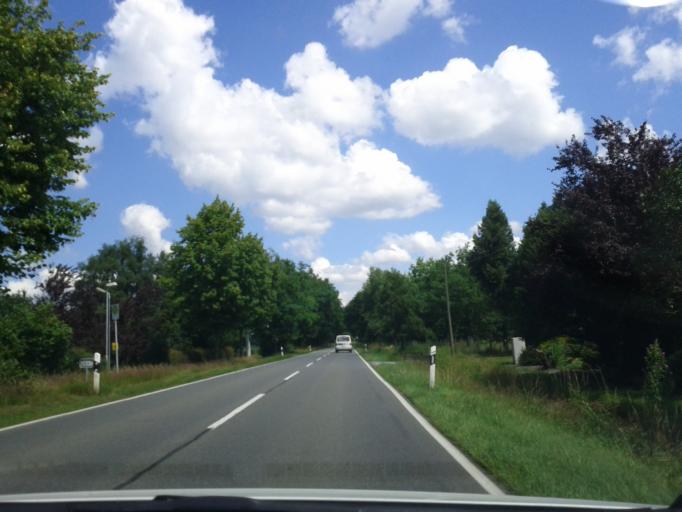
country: DE
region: Lower Saxony
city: Wohnste
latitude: 53.3336
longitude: 9.5335
